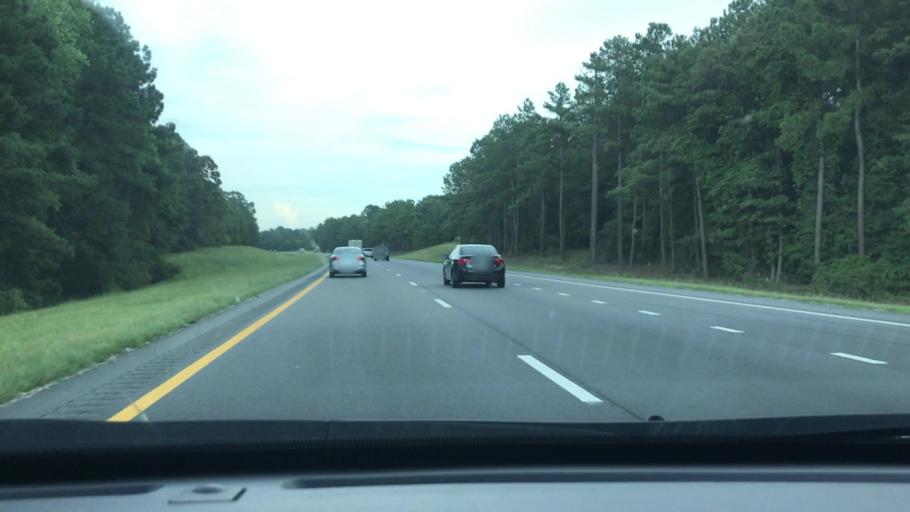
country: US
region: North Carolina
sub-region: Cumberland County
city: Hope Mills
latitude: 34.9406
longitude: -78.9162
